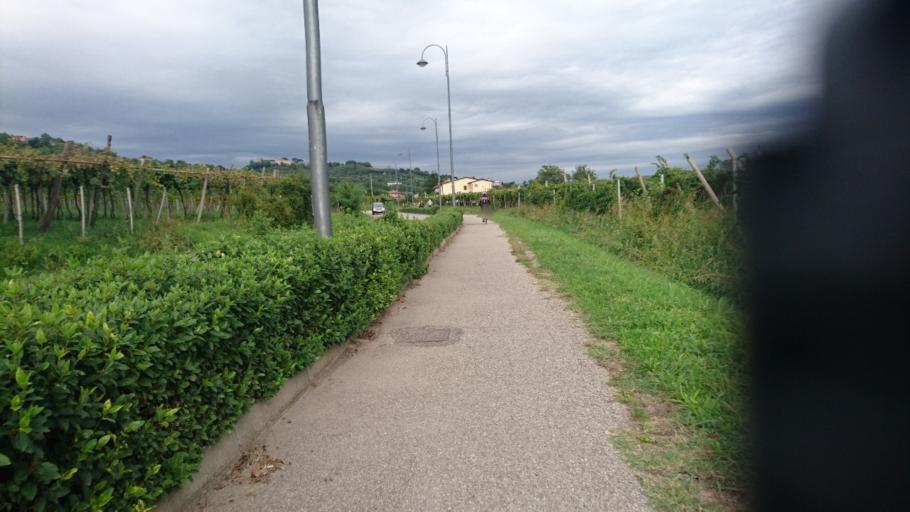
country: IT
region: Veneto
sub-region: Provincia di Vicenza
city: Montebello Vicentino
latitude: 45.4526
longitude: 11.3734
